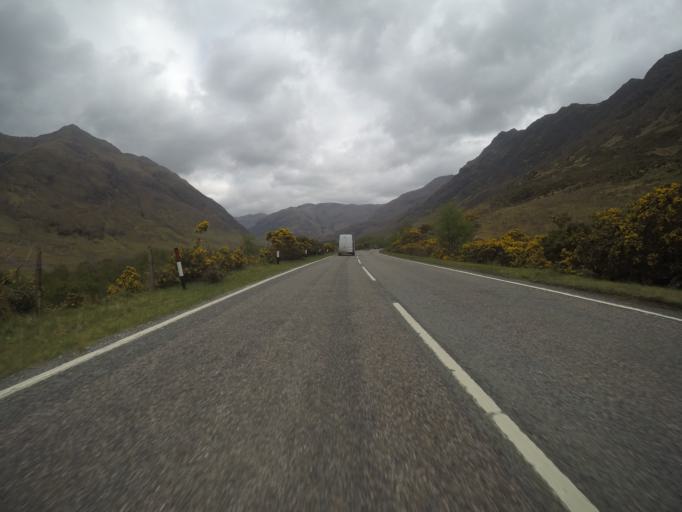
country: GB
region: Scotland
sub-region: Highland
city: Fort William
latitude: 57.1944
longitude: -5.3880
